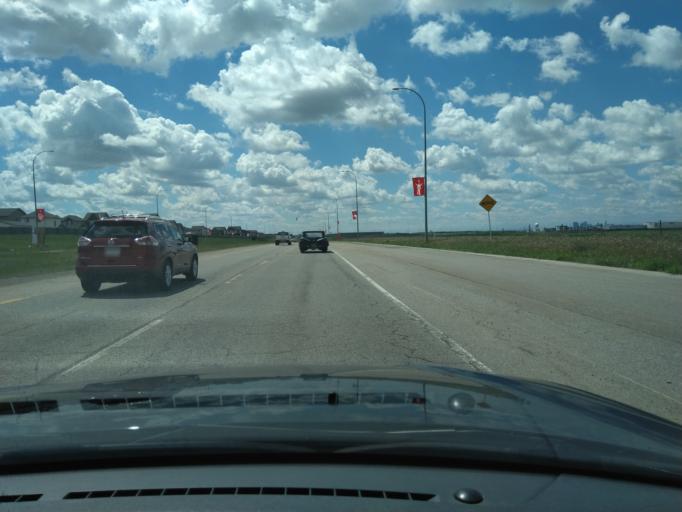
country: CA
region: Alberta
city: Airdrie
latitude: 51.1634
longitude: -113.9702
